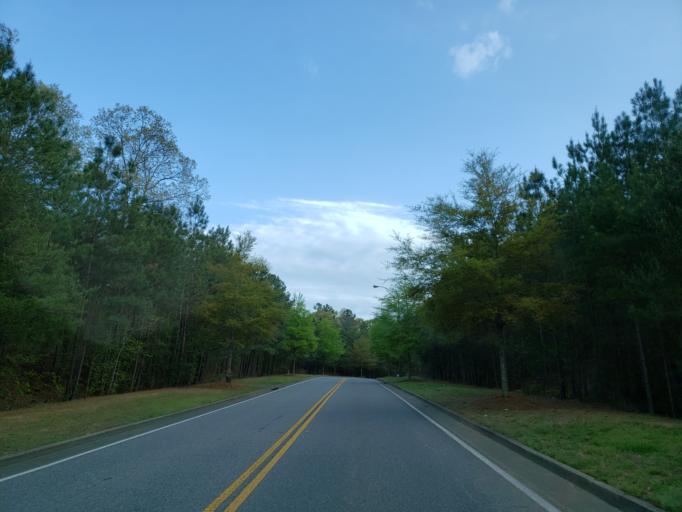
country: US
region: Georgia
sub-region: Cherokee County
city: Canton
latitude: 34.2905
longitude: -84.4633
